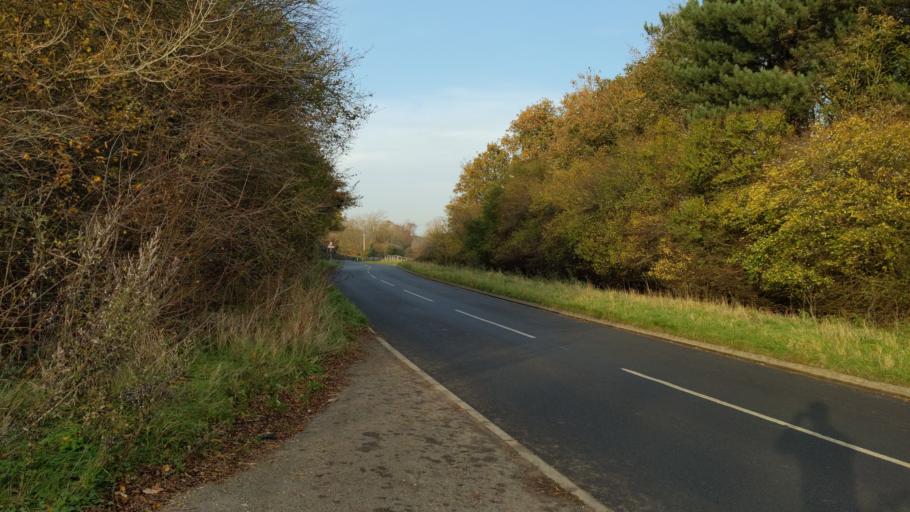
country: GB
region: England
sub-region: Milton Keynes
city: Shenley Church End
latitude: 51.9877
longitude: -0.8285
